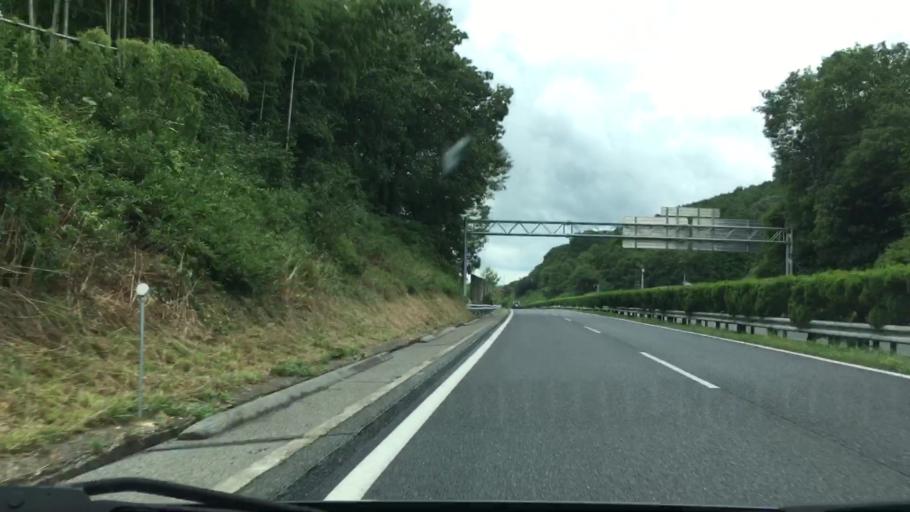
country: JP
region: Okayama
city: Tsuyama
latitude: 35.0407
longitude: 134.1256
